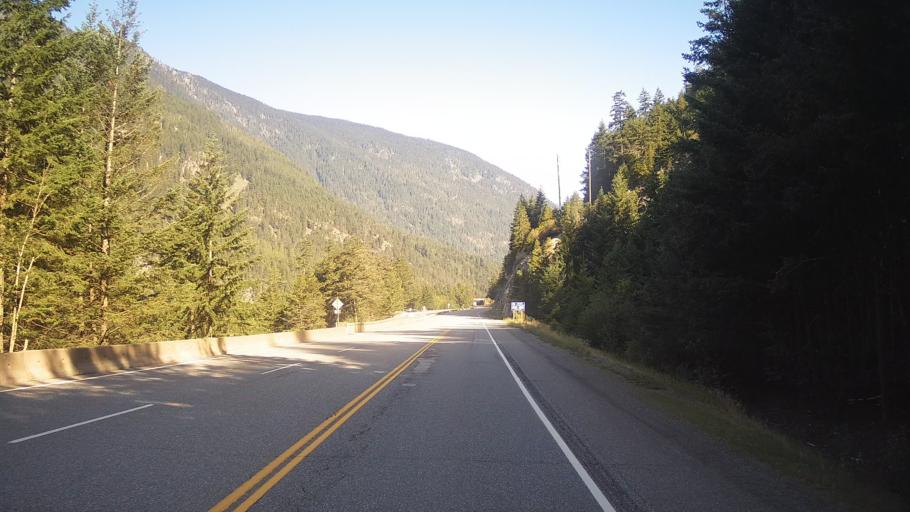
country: CA
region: British Columbia
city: Hope
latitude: 49.7754
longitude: -121.4395
